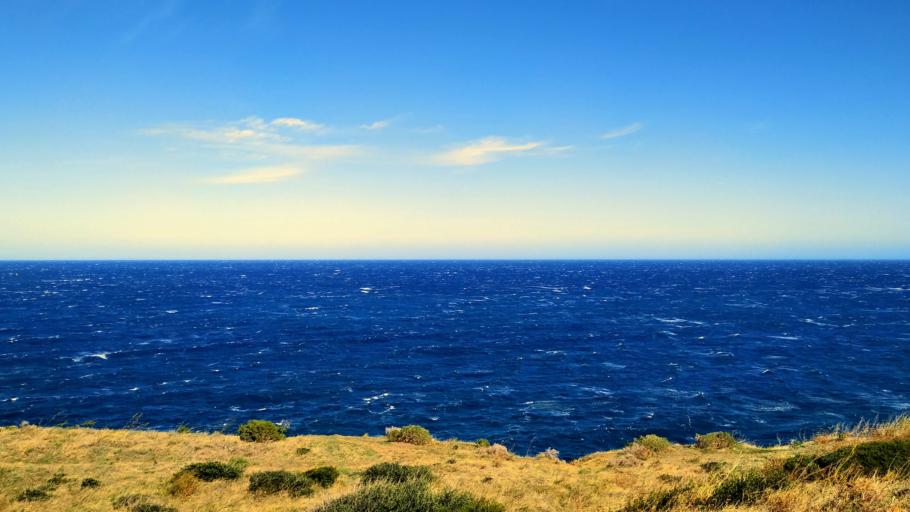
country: FR
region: Languedoc-Roussillon
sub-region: Departement des Pyrenees-Orientales
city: Cervera de la Marenda
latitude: 42.4404
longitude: 3.1756
